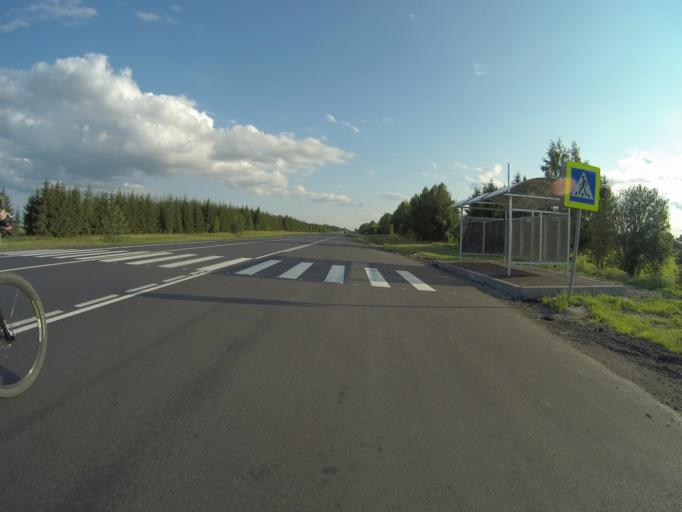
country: RU
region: Vladimir
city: Suzdal'
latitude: 56.4075
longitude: 40.4737
